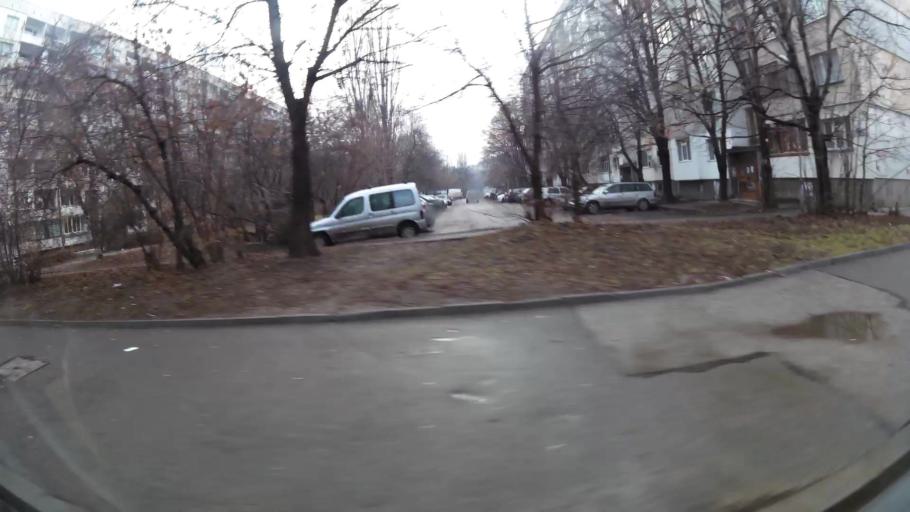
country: BG
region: Sofia-Capital
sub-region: Stolichna Obshtina
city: Sofia
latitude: 42.7255
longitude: 23.3072
